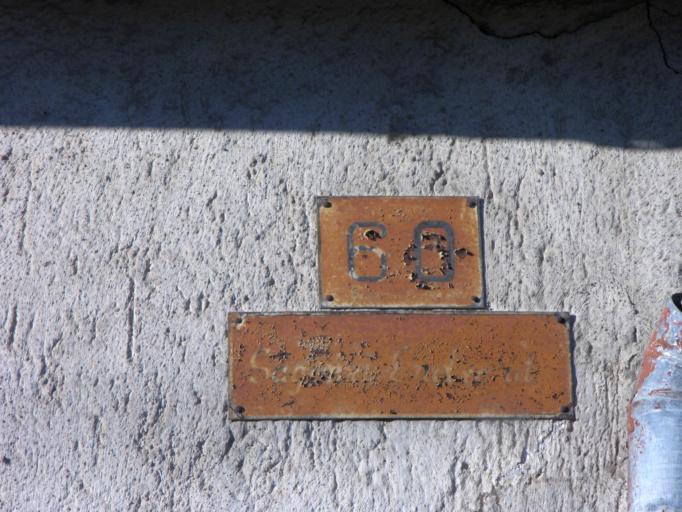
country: HU
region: Komarom-Esztergom
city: Labatlan
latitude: 47.7413
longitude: 18.5063
